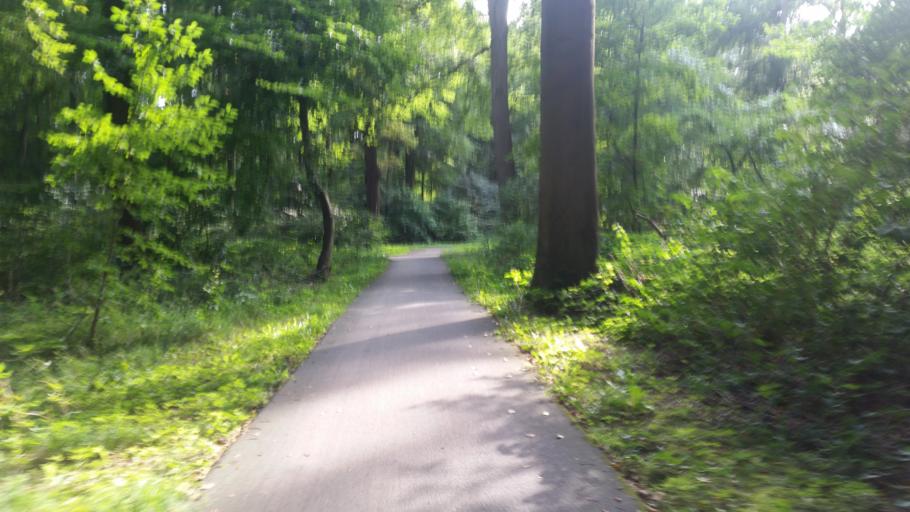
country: DE
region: Lower Saxony
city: Hannover
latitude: 52.3919
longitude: 9.7700
